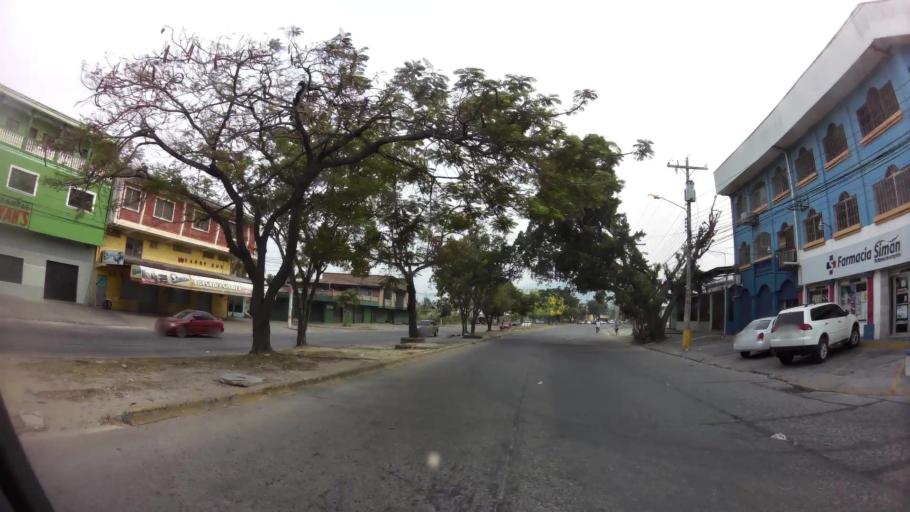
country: HN
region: Cortes
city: San Pedro Sula
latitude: 15.4927
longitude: -88.0163
